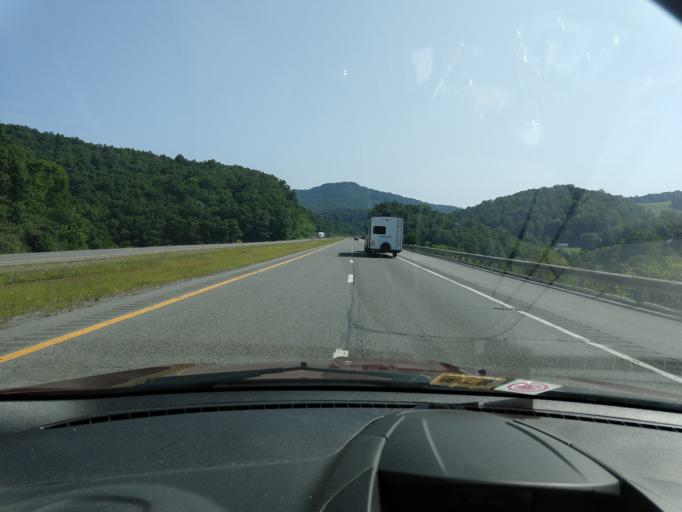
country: US
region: West Virginia
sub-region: Braxton County
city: Sutton
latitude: 38.6817
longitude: -80.7059
